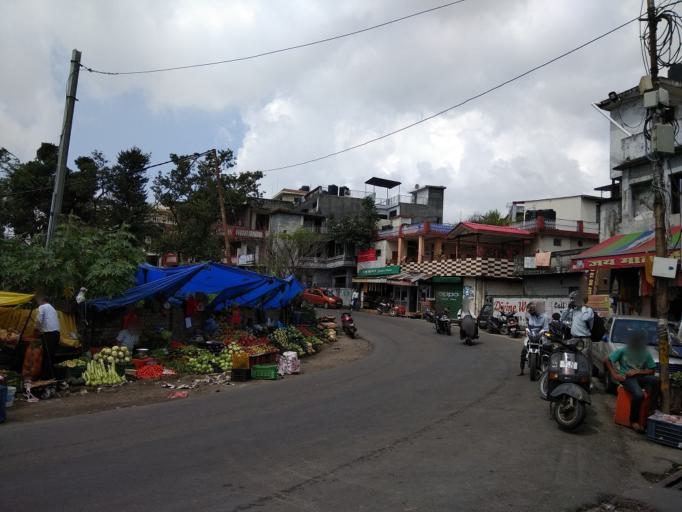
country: IN
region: Himachal Pradesh
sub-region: Kangra
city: Palampur
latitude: 32.1045
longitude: 76.5348
